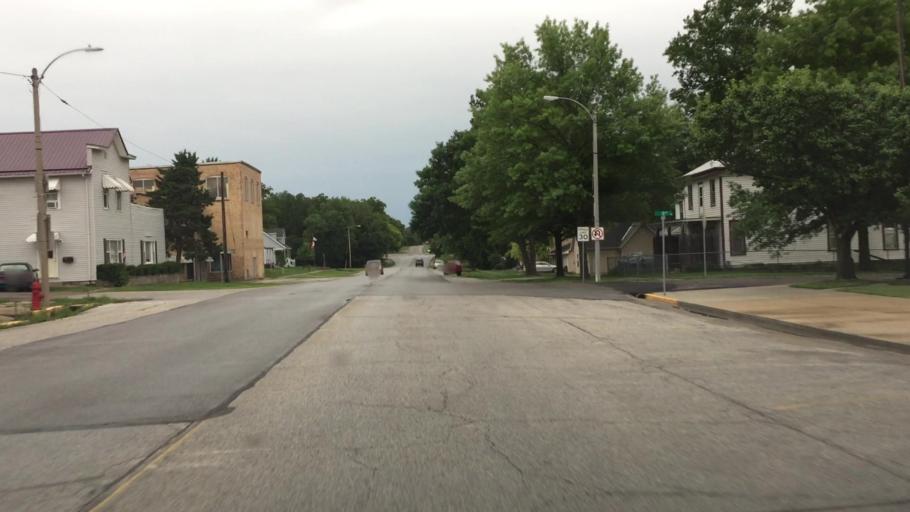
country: US
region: Illinois
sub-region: Hancock County
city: Hamilton
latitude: 40.3931
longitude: -91.3431
